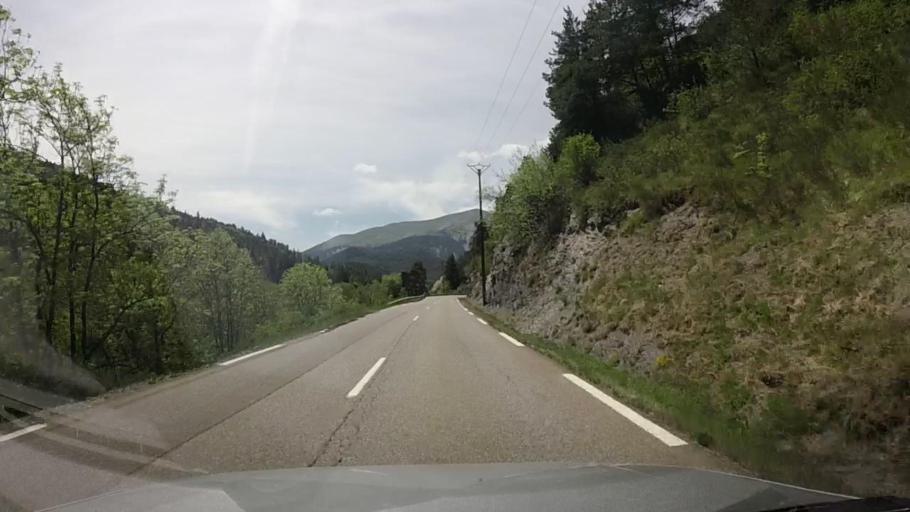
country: FR
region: Provence-Alpes-Cote d'Azur
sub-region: Departement des Alpes-de-Haute-Provence
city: Seyne-les-Alpes
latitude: 44.2681
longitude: 6.3720
